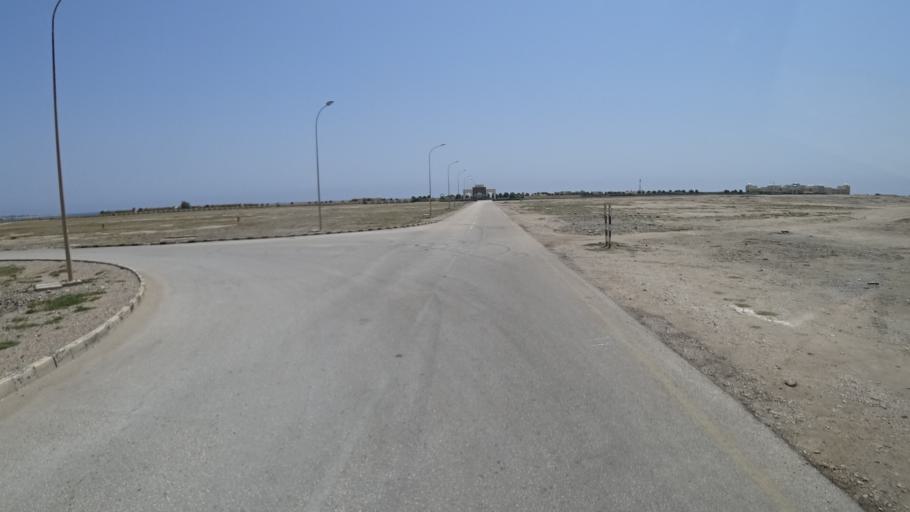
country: OM
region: Zufar
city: Salalah
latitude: 16.9638
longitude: 54.7387
